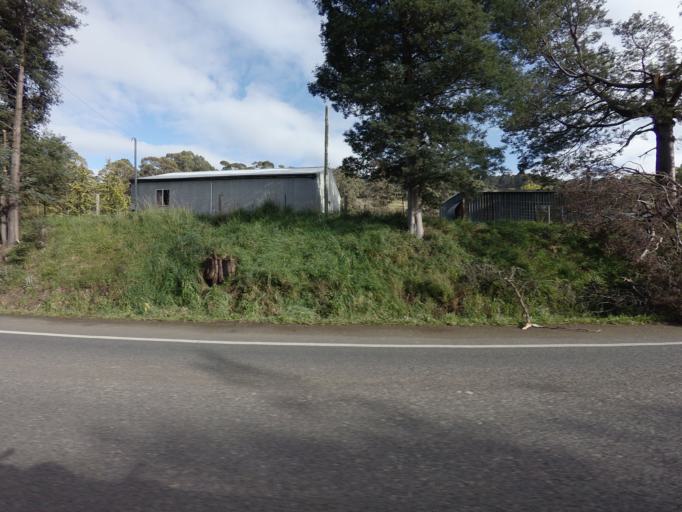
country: AU
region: Tasmania
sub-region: Huon Valley
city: Huonville
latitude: -43.0537
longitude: 147.0350
